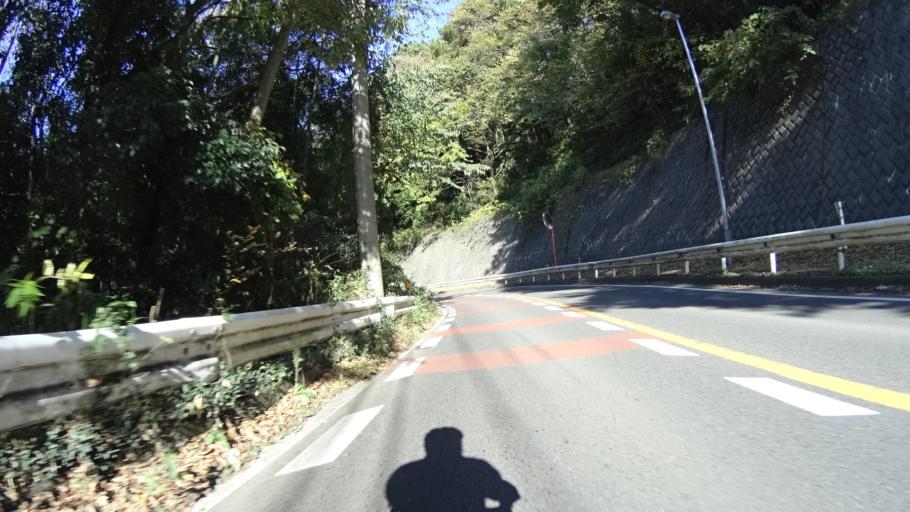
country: JP
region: Kanagawa
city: Zama
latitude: 35.5301
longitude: 139.3137
